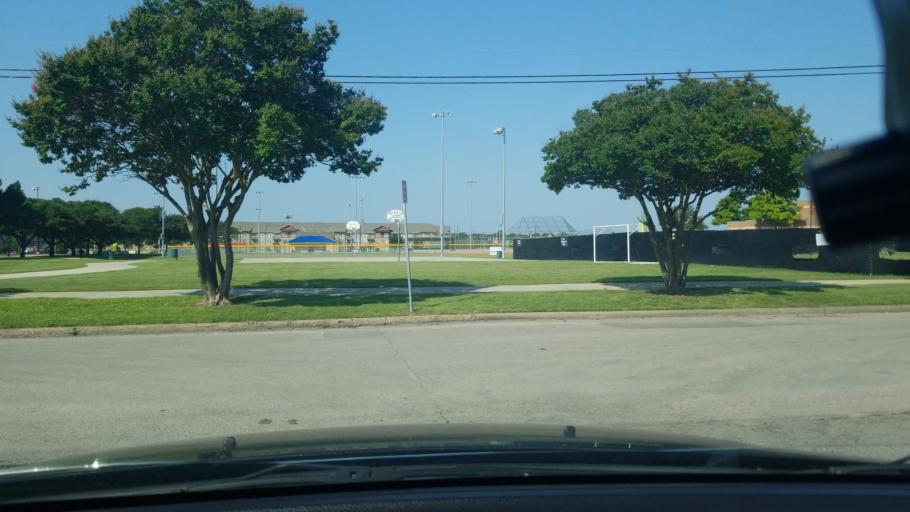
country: US
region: Texas
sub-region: Dallas County
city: Mesquite
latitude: 32.8277
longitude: -96.6435
